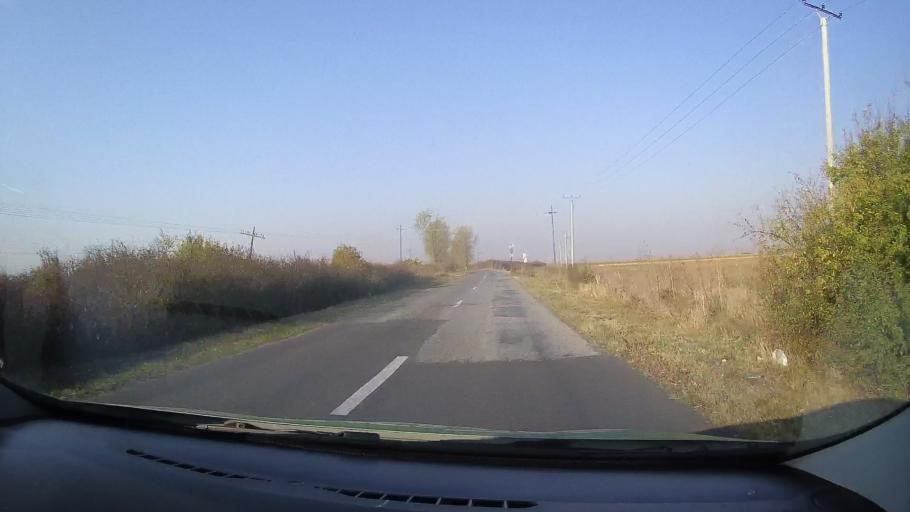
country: RO
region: Arad
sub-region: Comuna Graniceri
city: Siclau
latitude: 46.5010
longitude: 21.3957
